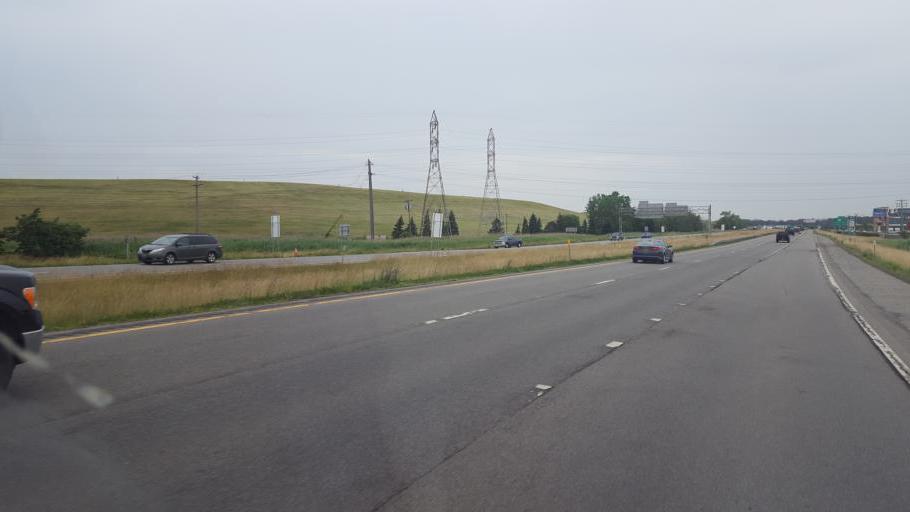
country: US
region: New York
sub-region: Niagara County
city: Niagara Falls
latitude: 43.0916
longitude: -78.9890
